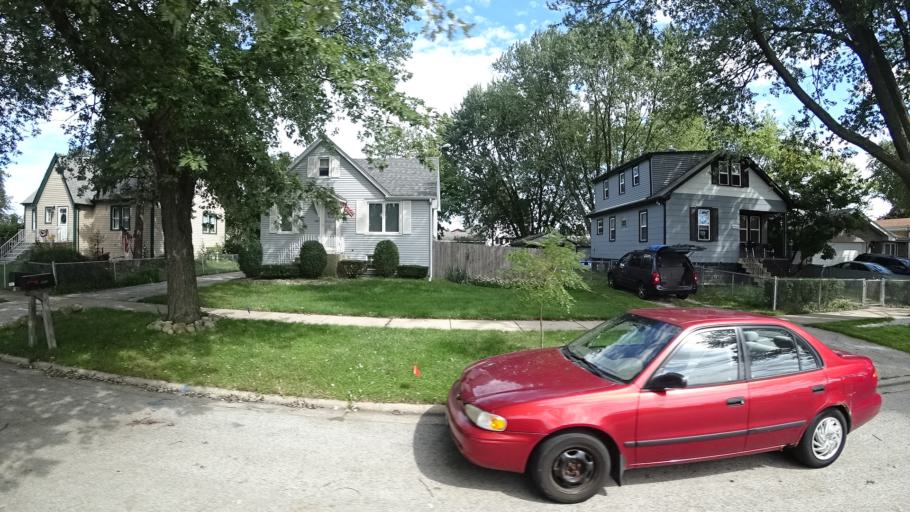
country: US
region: Illinois
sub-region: Cook County
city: Chicago Ridge
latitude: 41.7174
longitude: -87.7737
